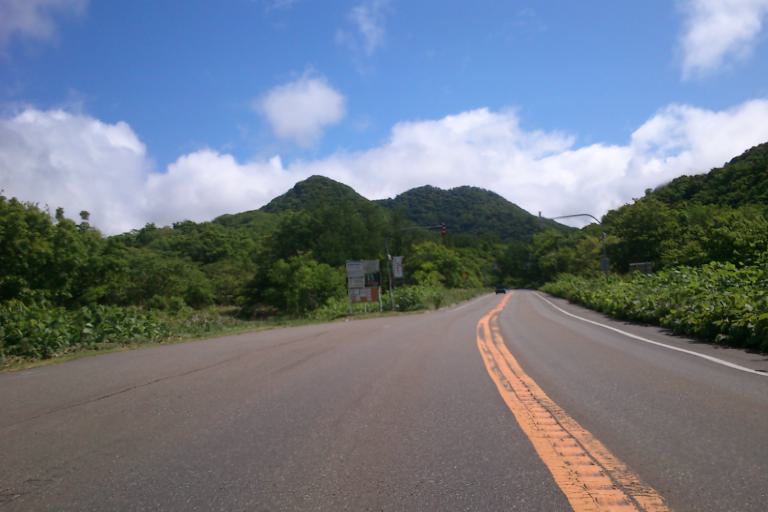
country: JP
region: Hokkaido
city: Ishikari
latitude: 43.4814
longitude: 141.3976
